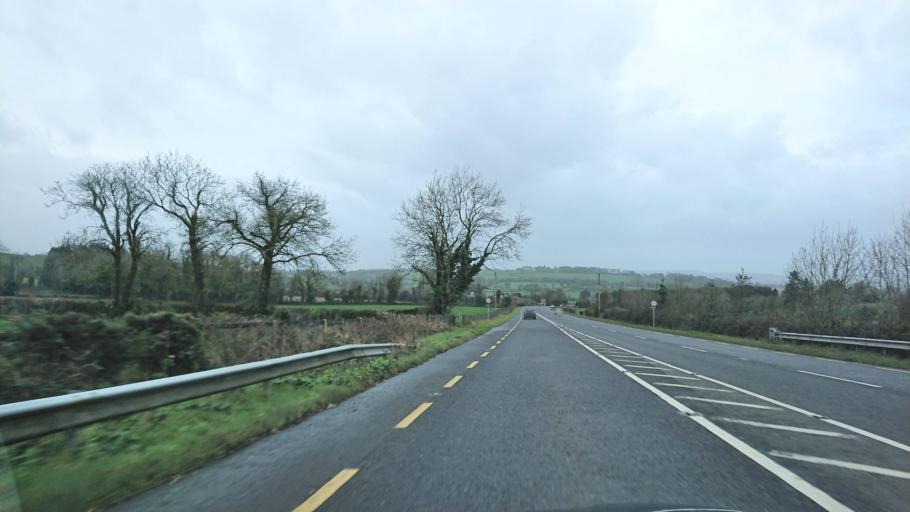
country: IE
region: Leinster
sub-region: Loch Garman
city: New Ross
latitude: 52.3847
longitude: -6.8875
